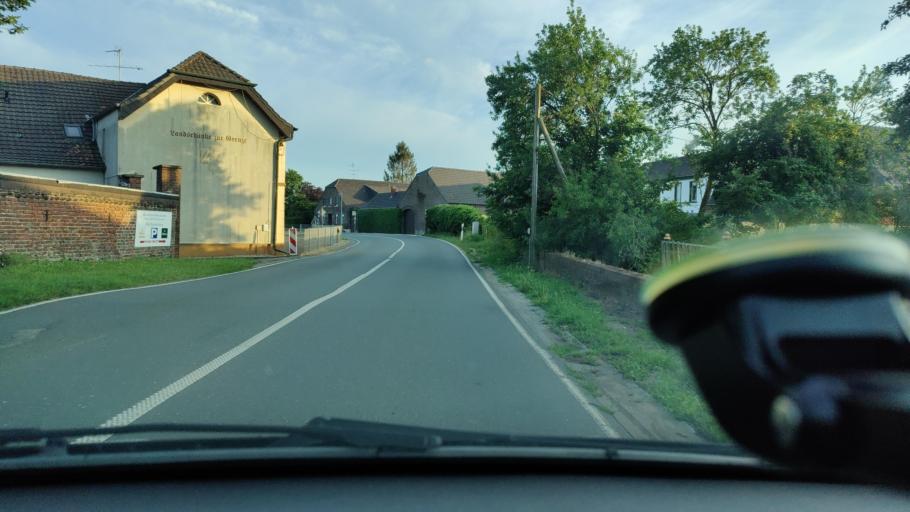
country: DE
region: North Rhine-Westphalia
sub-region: Regierungsbezirk Dusseldorf
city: Kamp-Lintfort
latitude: 51.4775
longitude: 6.5226
